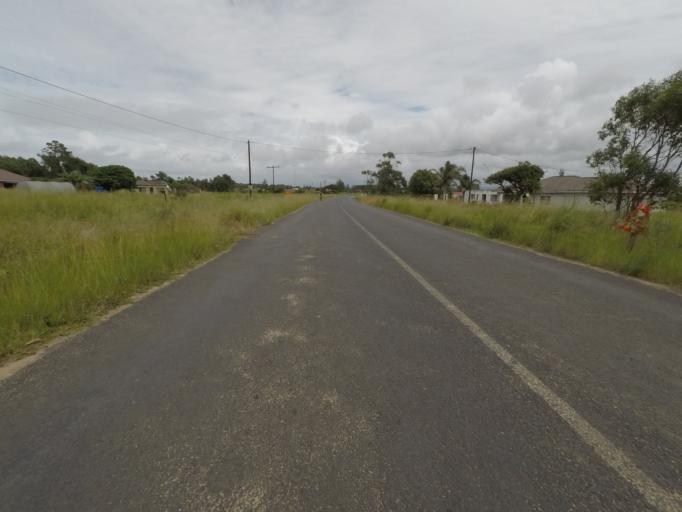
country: ZA
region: KwaZulu-Natal
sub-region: uThungulu District Municipality
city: eSikhawini
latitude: -28.9100
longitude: 31.8722
